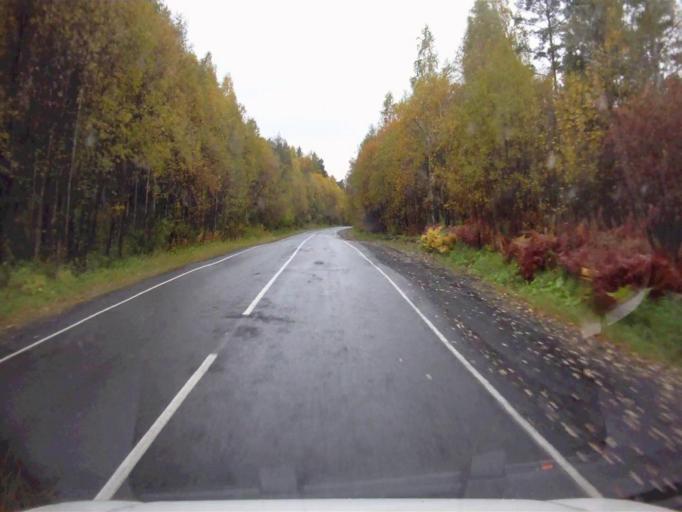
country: RU
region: Chelyabinsk
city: Verkhniy Ufaley
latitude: 56.0448
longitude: 60.1104
